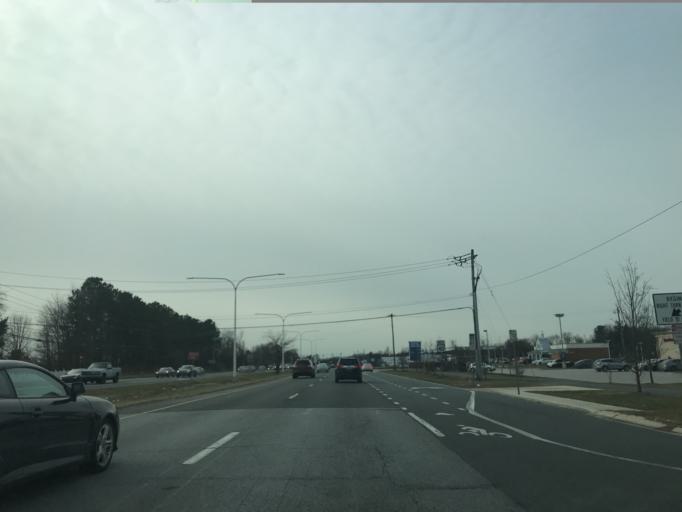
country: US
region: Delaware
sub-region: New Castle County
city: Bear
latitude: 39.6228
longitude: -75.6839
